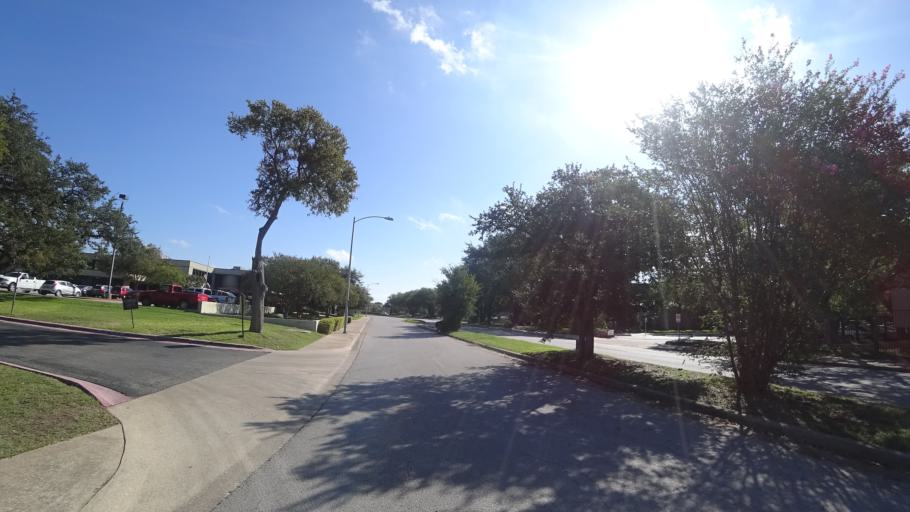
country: US
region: Texas
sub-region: Travis County
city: Austin
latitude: 30.3254
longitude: -97.7034
